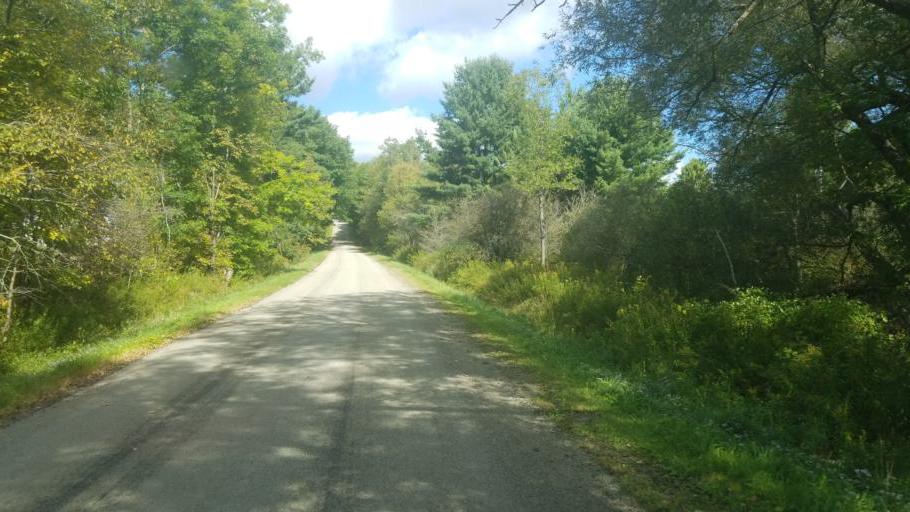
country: US
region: New York
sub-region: Allegany County
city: Cuba
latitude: 42.1947
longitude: -78.3089
